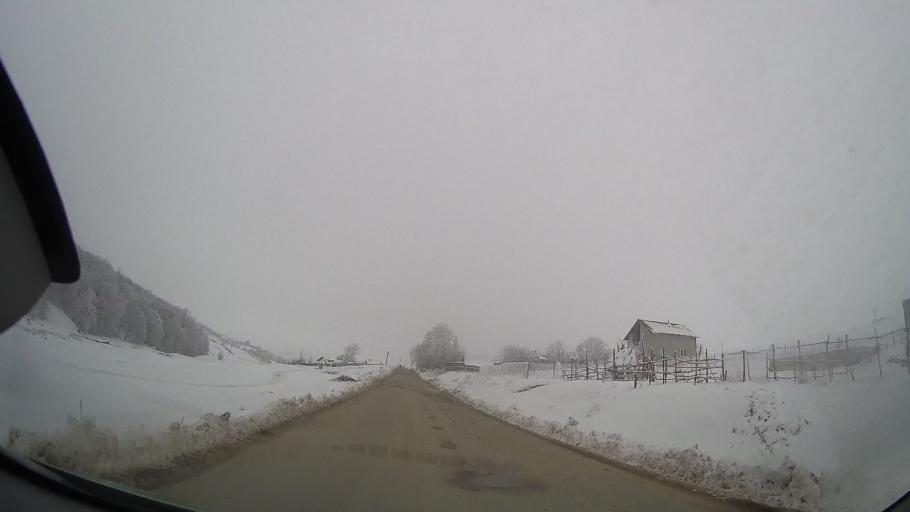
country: RO
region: Neamt
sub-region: Comuna Pancesti
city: Pancesti
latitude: 46.9119
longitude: 27.1597
